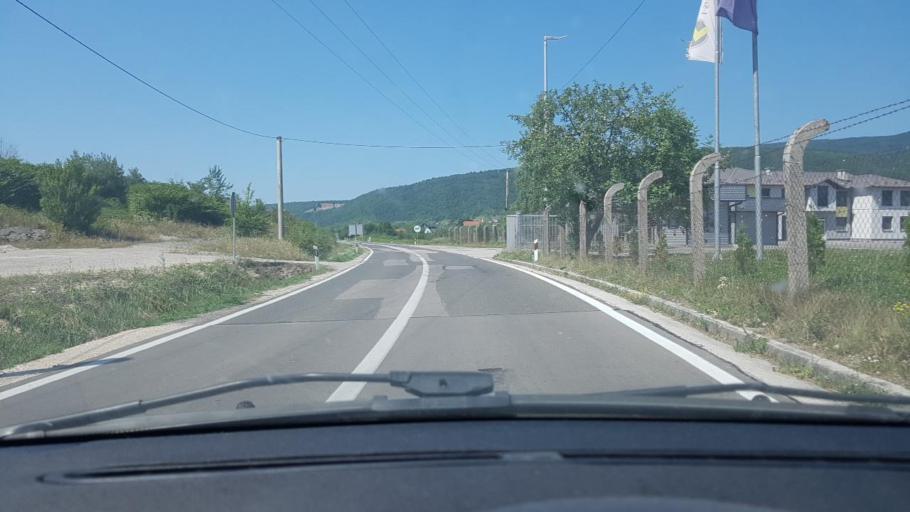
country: BA
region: Federation of Bosnia and Herzegovina
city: Bihac
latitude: 44.7637
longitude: 15.9448
